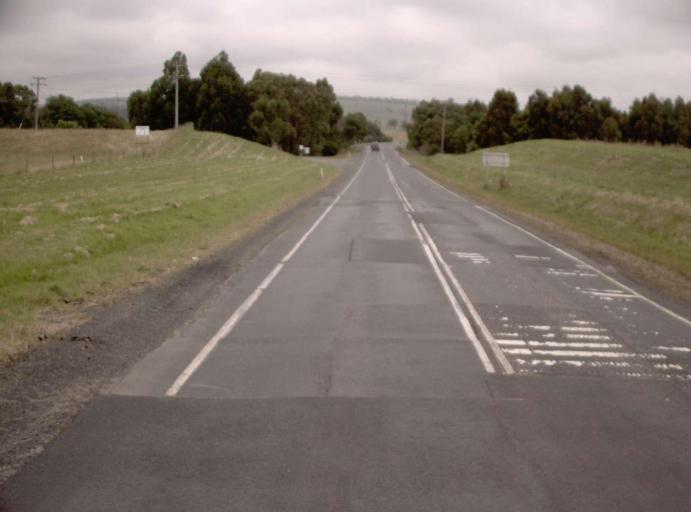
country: AU
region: Victoria
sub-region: Latrobe
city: Traralgon
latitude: -38.2494
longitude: 146.5453
